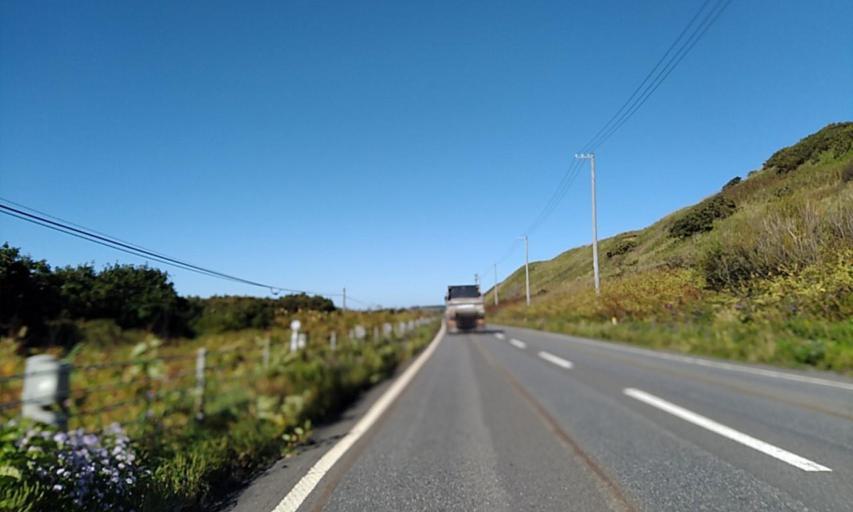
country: JP
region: Hokkaido
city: Shizunai-furukawacho
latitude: 42.4681
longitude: 142.1362
